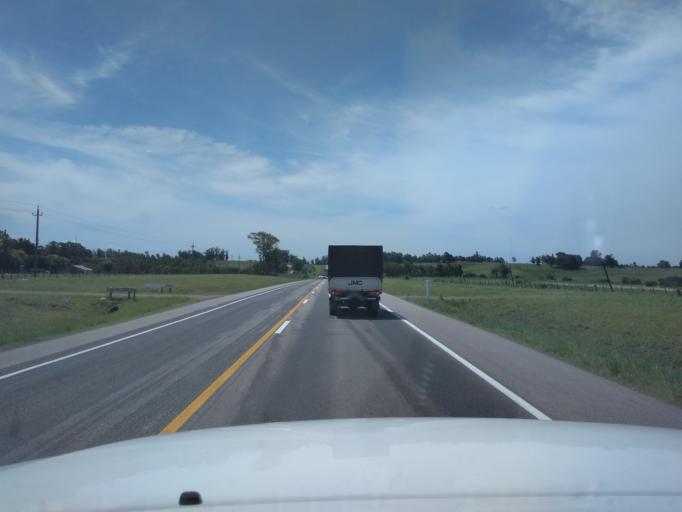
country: UY
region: Florida
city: Florida
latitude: -34.1312
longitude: -56.1852
